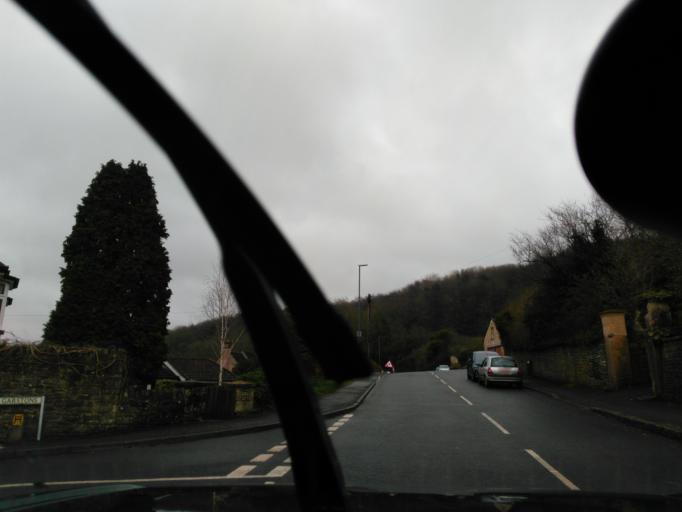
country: GB
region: England
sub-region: Wiltshire
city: Colerne
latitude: 51.3990
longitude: -2.2943
